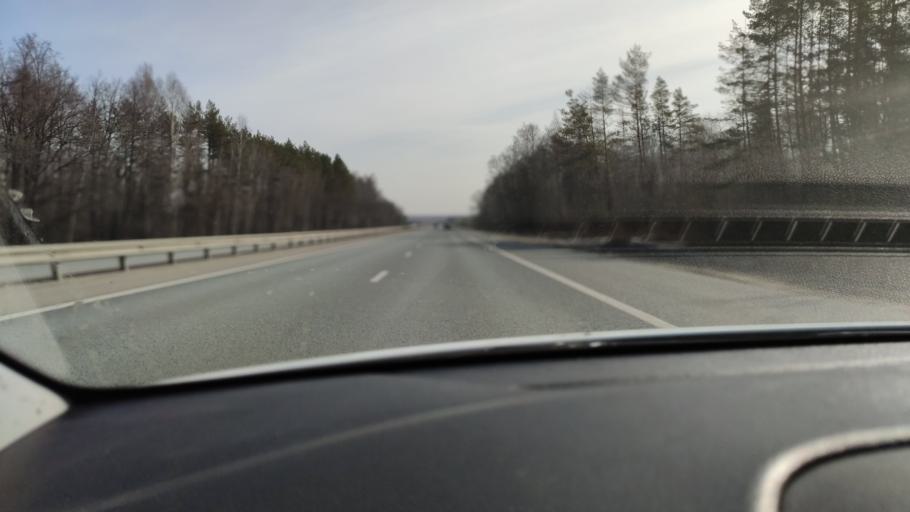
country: RU
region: Tatarstan
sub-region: Gorod Kazan'
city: Kazan
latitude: 55.9115
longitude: 49.0837
